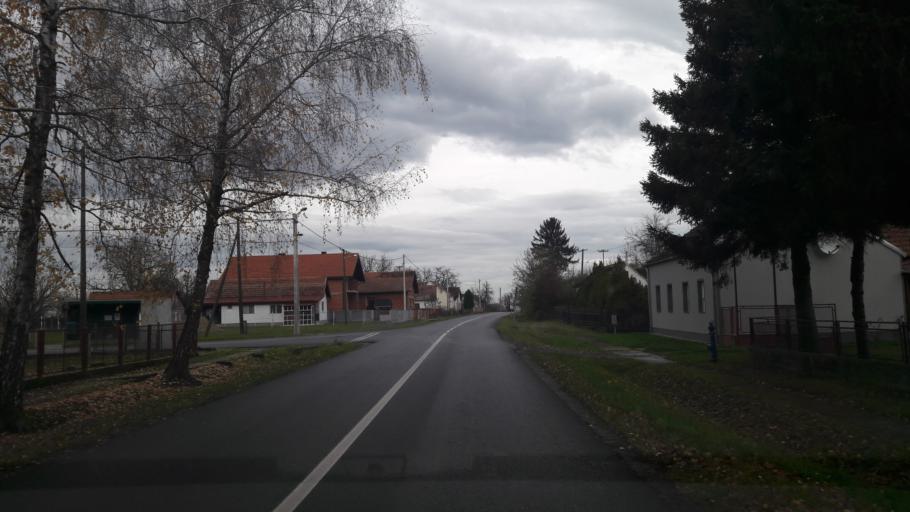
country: HR
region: Osjecko-Baranjska
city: Martin
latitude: 45.5322
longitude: 18.0601
